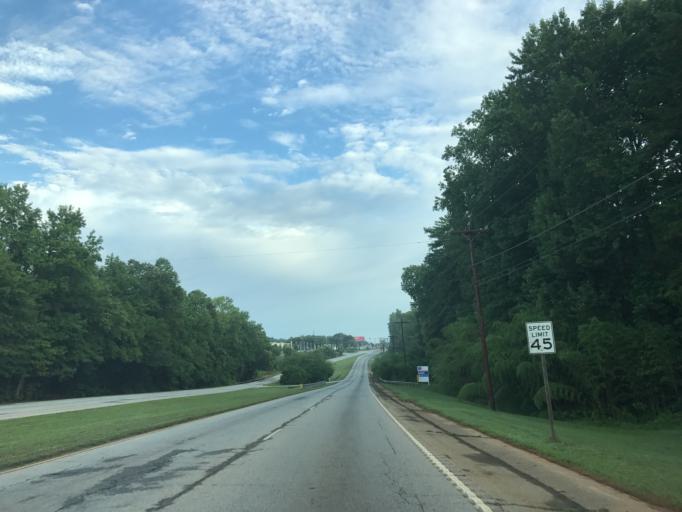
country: US
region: South Carolina
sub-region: Greenville County
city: Mauldin
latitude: 34.8054
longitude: -82.3257
